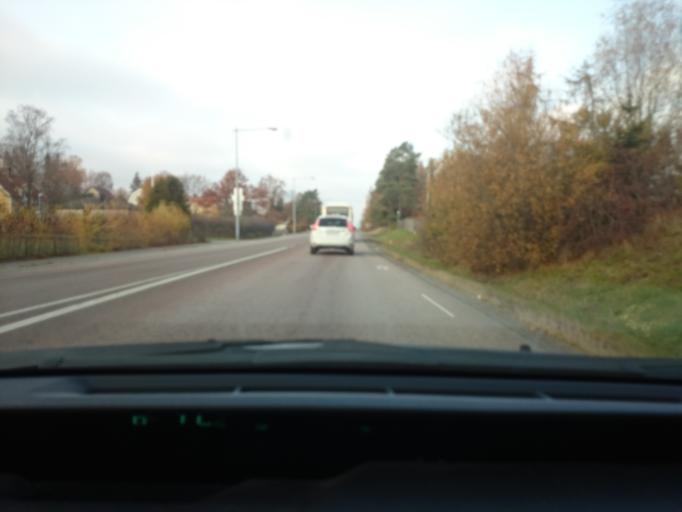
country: SE
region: Vaestmanland
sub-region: Vasteras
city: Vasteras
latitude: 59.6383
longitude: 16.5107
